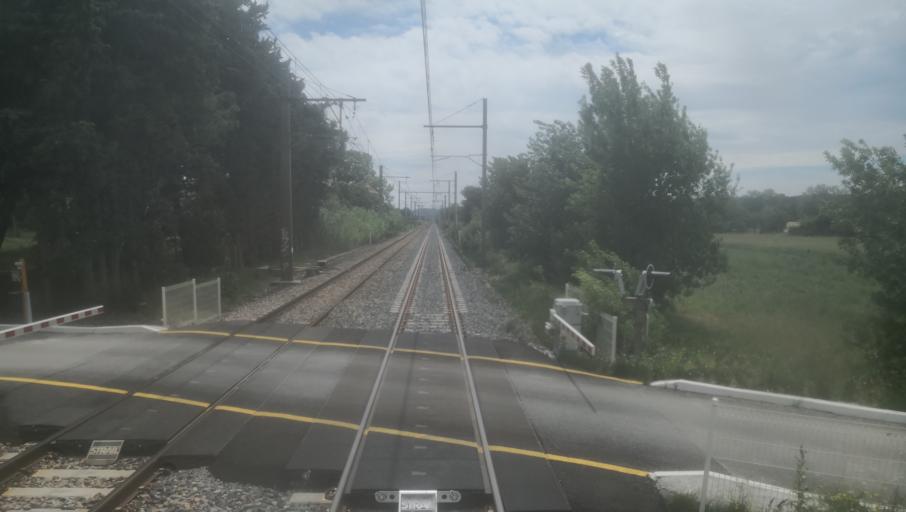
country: FR
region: Languedoc-Roussillon
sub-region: Departement de l'Herault
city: Mireval
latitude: 43.5246
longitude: 3.8318
